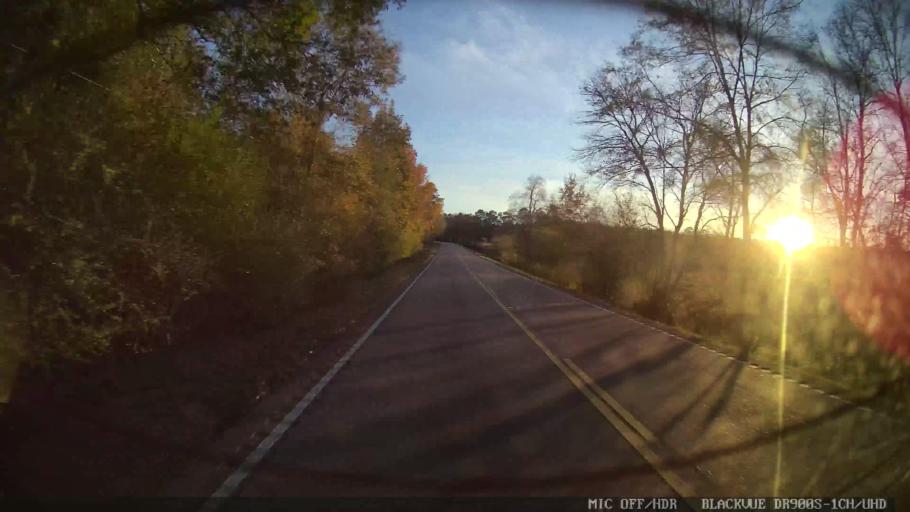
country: US
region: Mississippi
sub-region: Stone County
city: Wiggins
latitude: 31.0125
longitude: -89.2560
